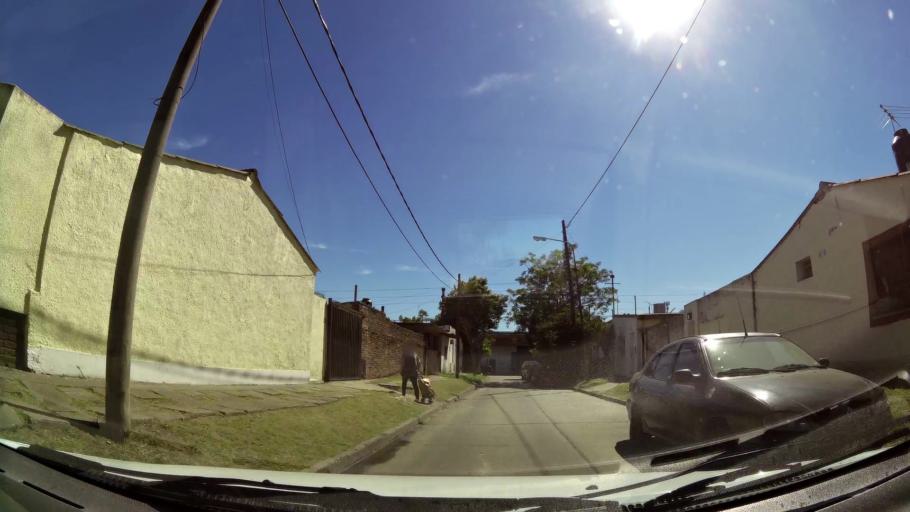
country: AR
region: Buenos Aires
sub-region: Partido de General San Martin
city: General San Martin
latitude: -34.5441
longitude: -58.5308
